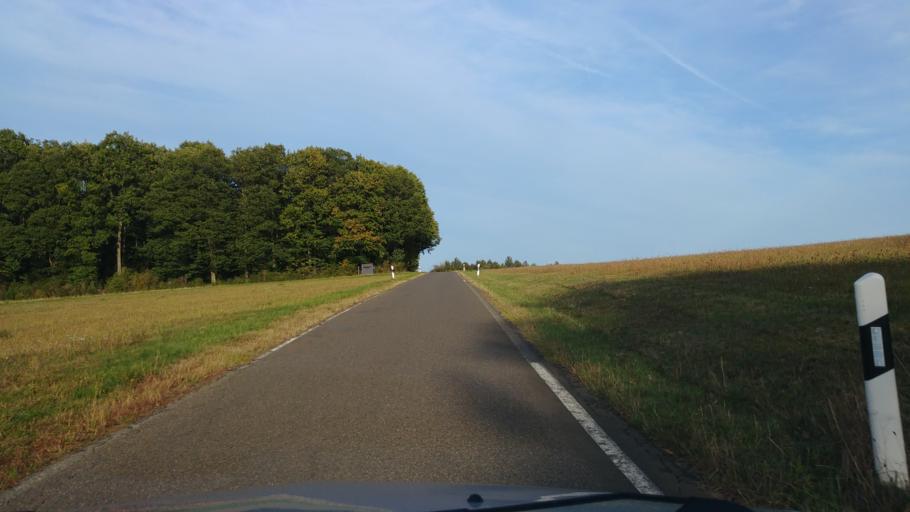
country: DE
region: Rheinland-Pfalz
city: Merschbach
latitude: 49.8172
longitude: 7.0149
